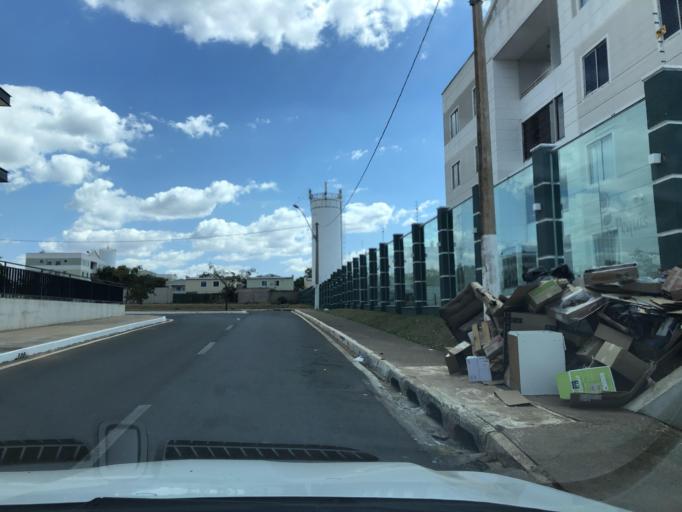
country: BR
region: Federal District
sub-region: Brasilia
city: Brasilia
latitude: -15.8885
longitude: -47.8152
